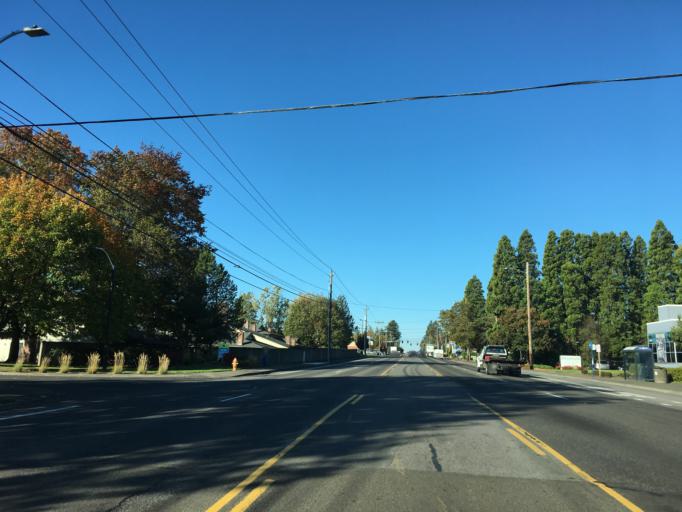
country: US
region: Oregon
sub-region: Multnomah County
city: Wood Village
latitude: 45.5191
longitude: -122.4087
